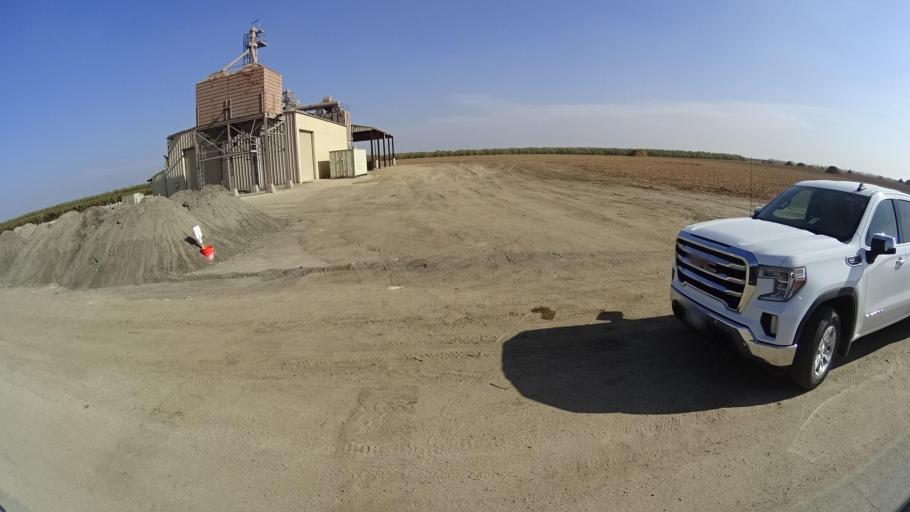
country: US
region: California
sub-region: Kern County
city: Shafter
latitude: 35.5435
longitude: -119.1335
